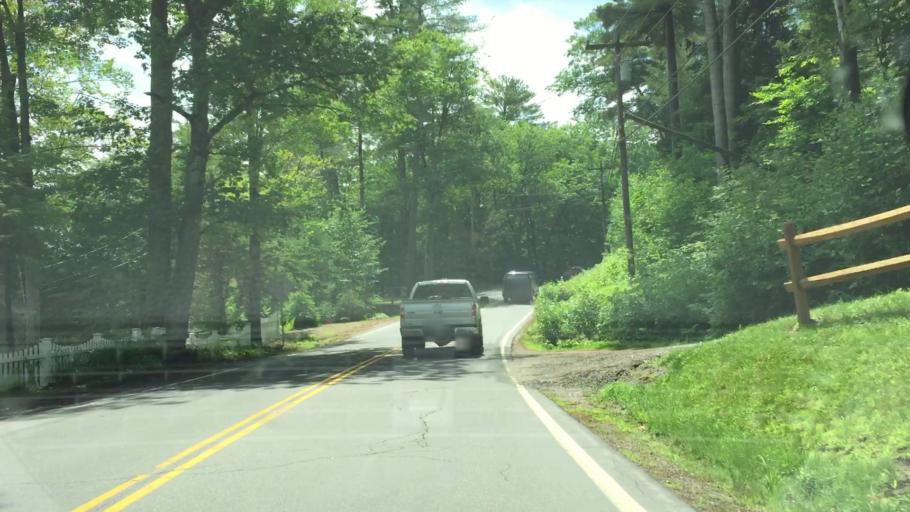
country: US
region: New Hampshire
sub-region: Grafton County
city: Holderness
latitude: 43.7362
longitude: -71.5860
